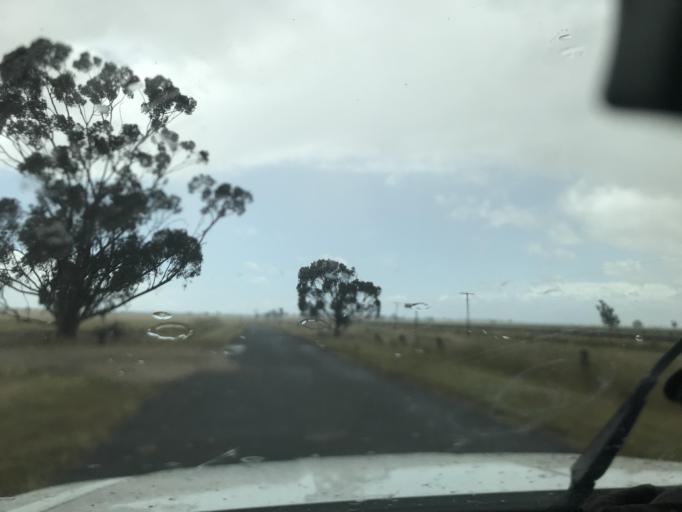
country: AU
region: South Australia
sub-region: Tatiara
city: Bordertown
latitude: -36.3751
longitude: 140.9925
